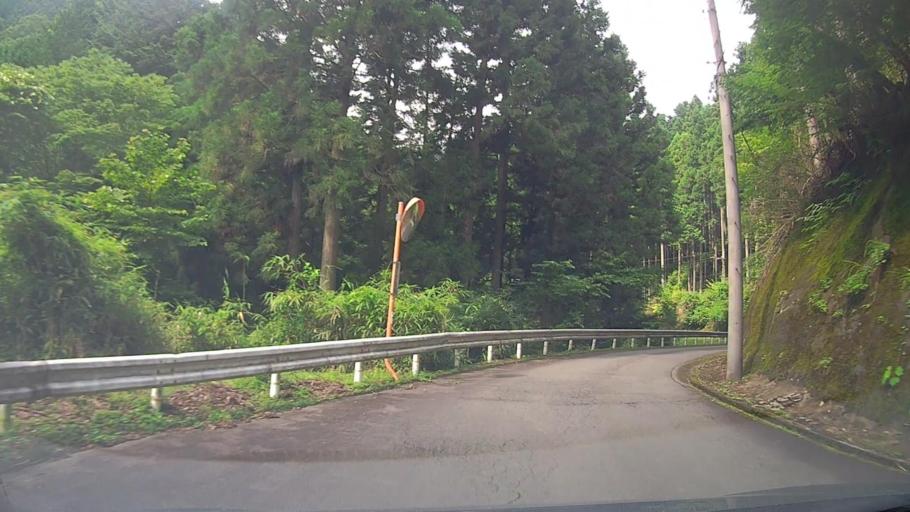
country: JP
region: Yamanashi
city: Uenohara
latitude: 35.7446
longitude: 139.0803
